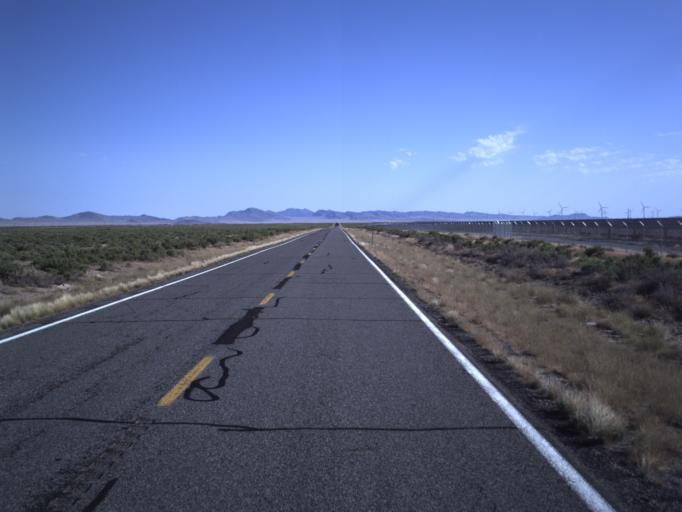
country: US
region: Utah
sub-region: Beaver County
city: Milford
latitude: 38.5067
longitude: -112.9911
